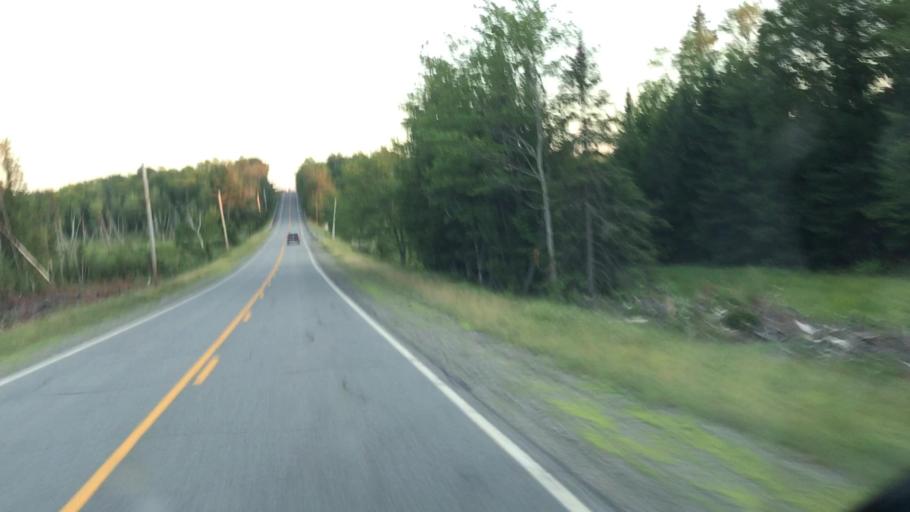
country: US
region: Maine
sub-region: Penobscot County
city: Medway
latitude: 45.5997
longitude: -68.3097
